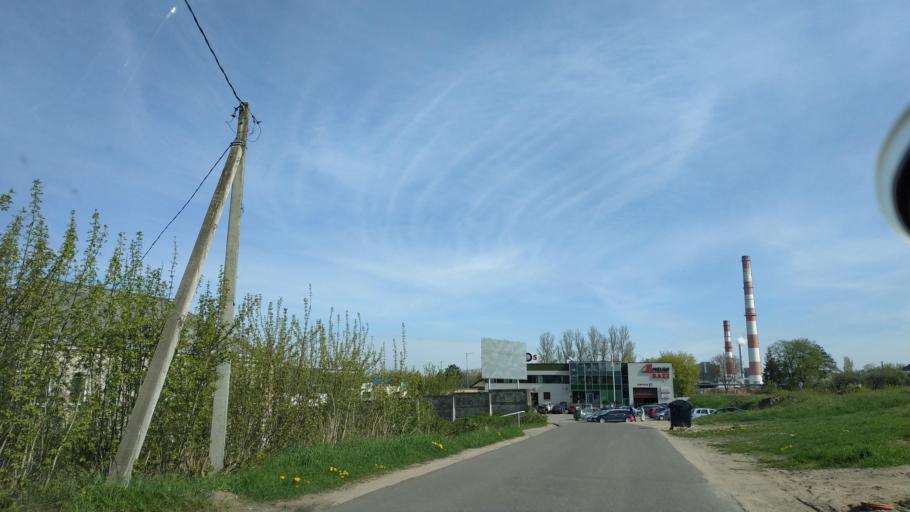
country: LT
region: Vilnius County
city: Vilkpede
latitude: 54.6578
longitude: 25.2284
